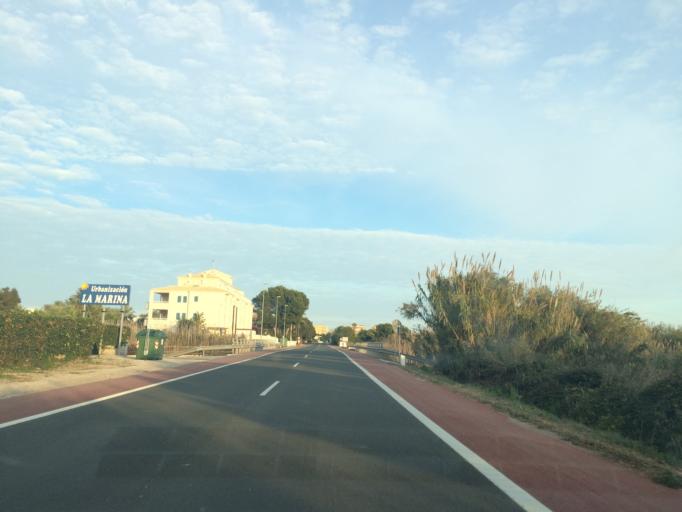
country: ES
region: Valencia
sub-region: Provincia de Alicante
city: els Poblets
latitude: 38.8584
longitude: 0.0420
